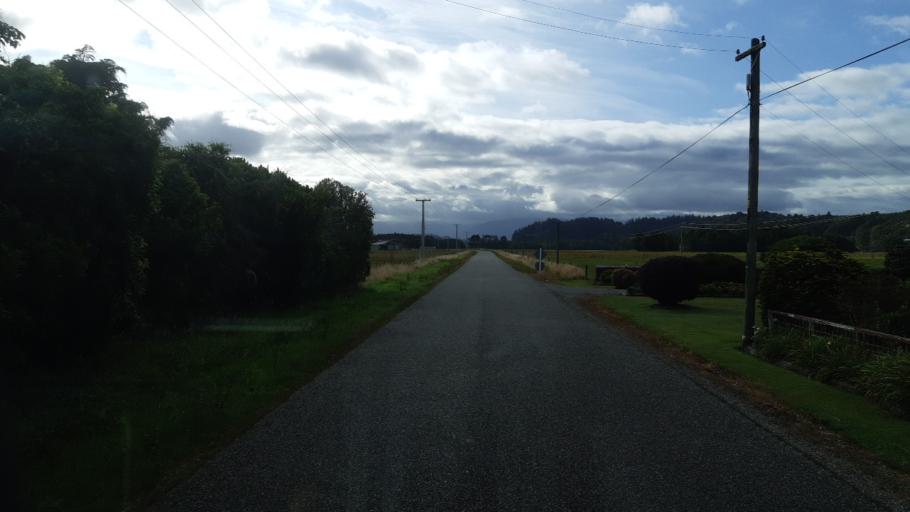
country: NZ
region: West Coast
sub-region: Westland District
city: Hokitika
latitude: -42.7334
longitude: 170.9666
